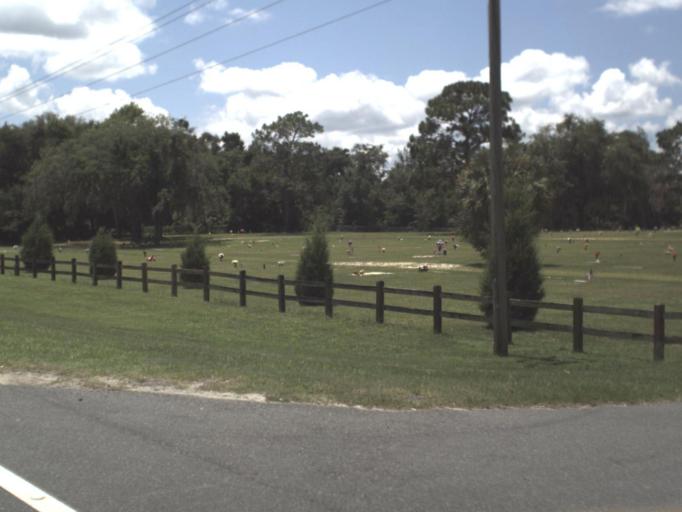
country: US
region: Florida
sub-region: Clay County
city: Keystone Heights
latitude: 29.7941
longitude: -82.0450
